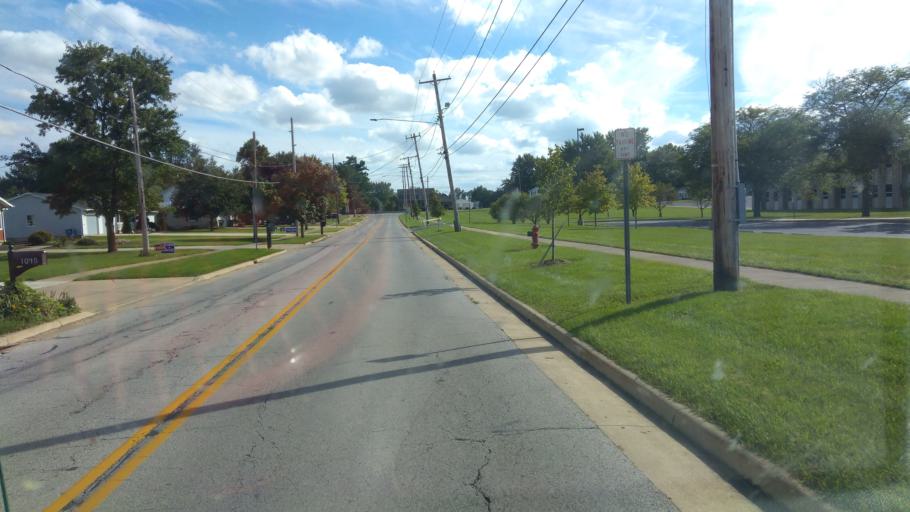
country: US
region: Ohio
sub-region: Sandusky County
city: Clyde
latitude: 41.2904
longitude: -82.9848
